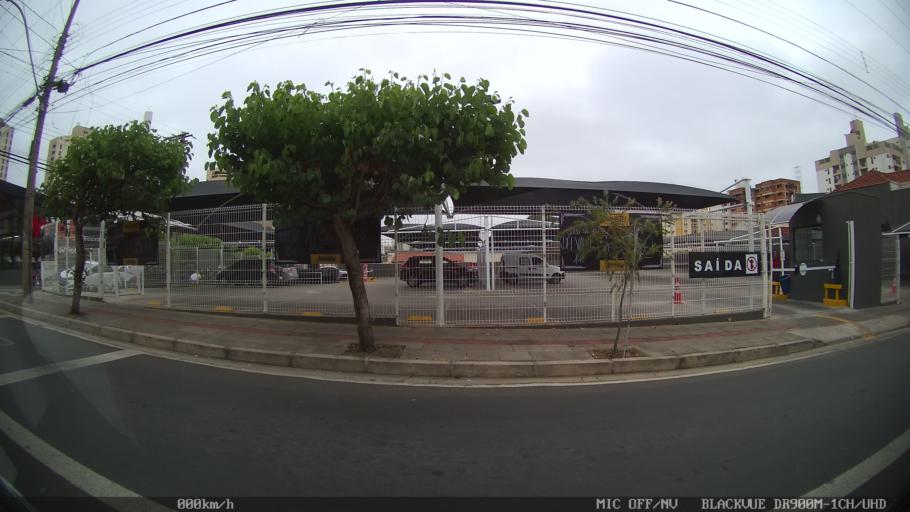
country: BR
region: Sao Paulo
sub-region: Sao Jose Do Rio Preto
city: Sao Jose do Rio Preto
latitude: -20.8183
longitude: -49.3895
